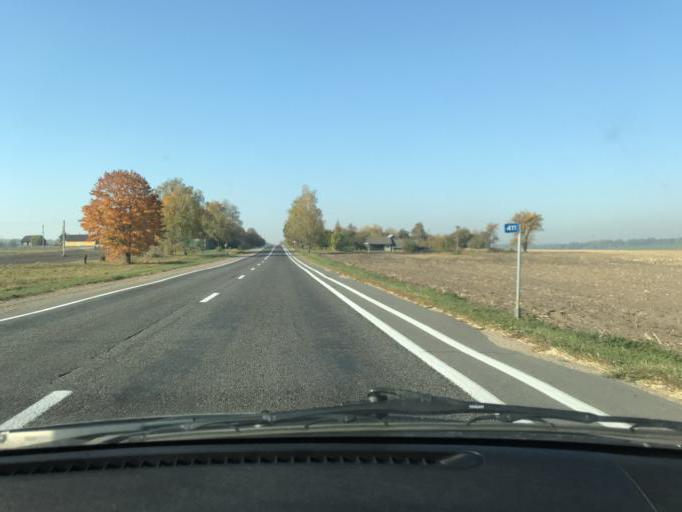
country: BY
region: Minsk
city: Klyetsk
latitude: 52.9708
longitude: 26.6618
